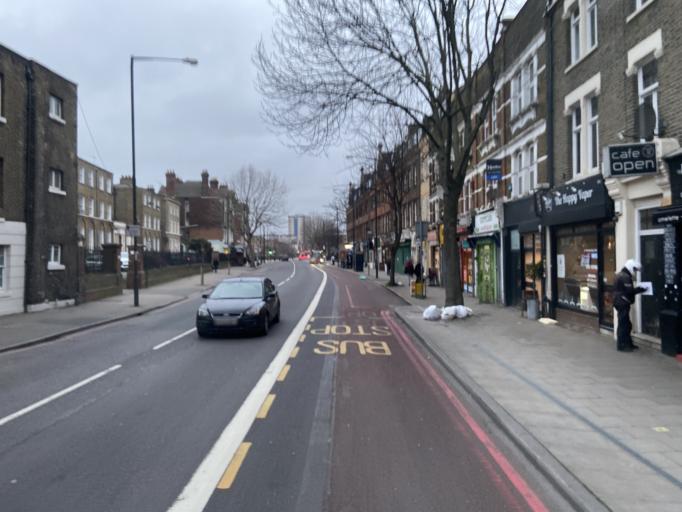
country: GB
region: England
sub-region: Greater London
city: Hackney
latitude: 51.5533
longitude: -0.0534
